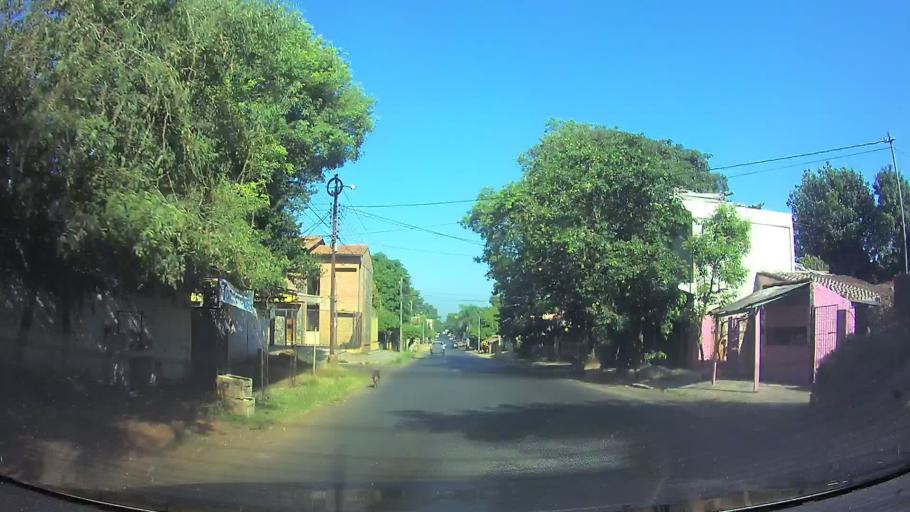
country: PY
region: Central
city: San Lorenzo
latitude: -25.2764
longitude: -57.5013
